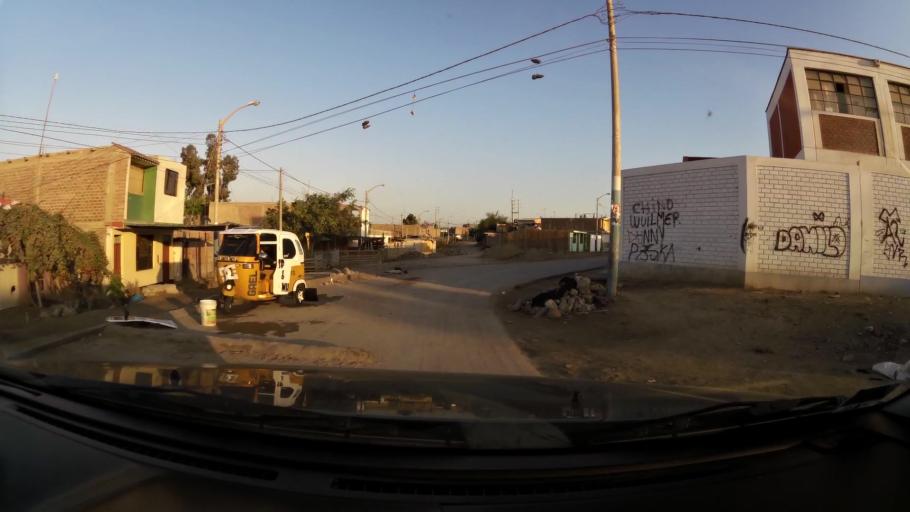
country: PE
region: Ica
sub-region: Provincia de Pisco
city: Villa Tupac Amaru
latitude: -13.6999
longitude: -76.1532
